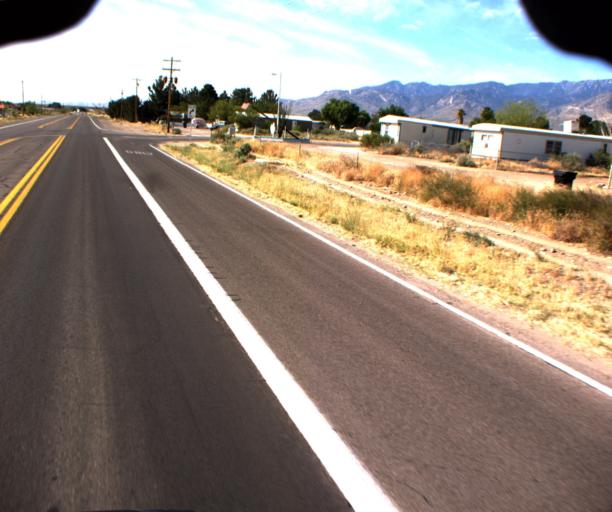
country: US
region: Arizona
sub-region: Graham County
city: Swift Trail Junction
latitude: 32.7435
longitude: -109.7164
